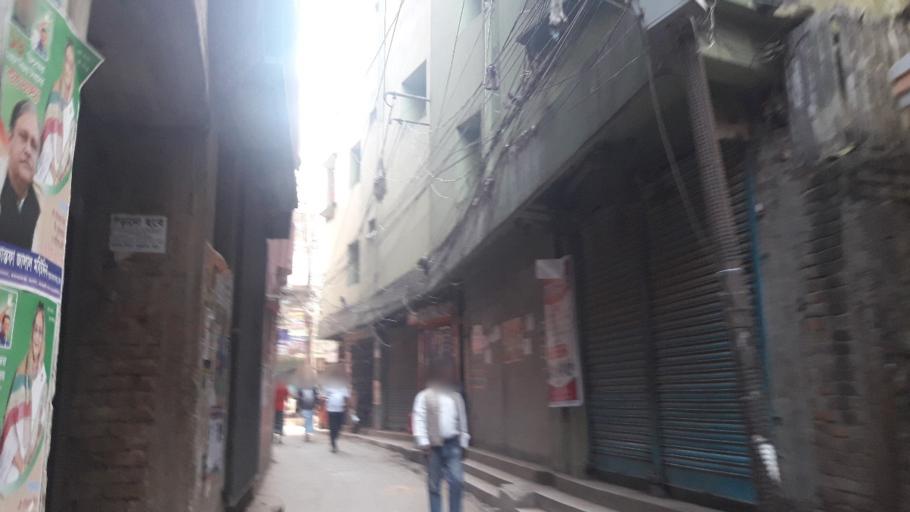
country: BD
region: Dhaka
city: Azimpur
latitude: 23.7237
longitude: 90.3761
